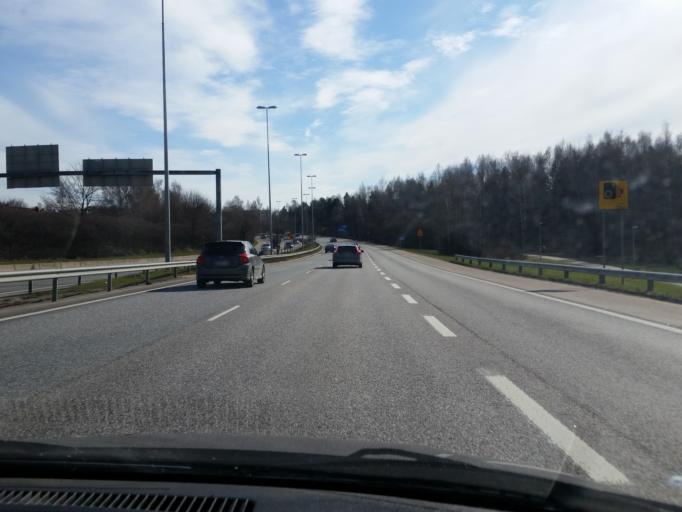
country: FI
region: Uusimaa
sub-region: Helsinki
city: Helsinki
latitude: 60.2179
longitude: 24.9444
